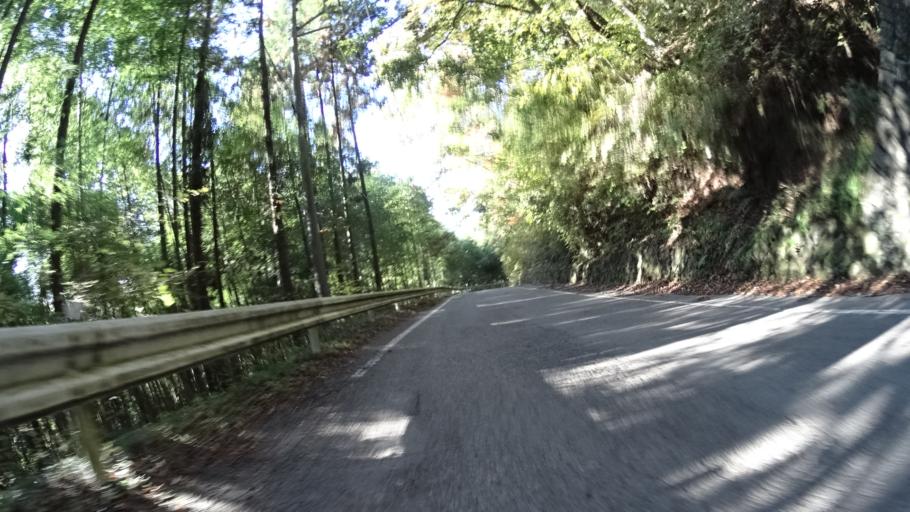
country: JP
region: Yamanashi
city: Uenohara
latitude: 35.6777
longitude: 139.0952
